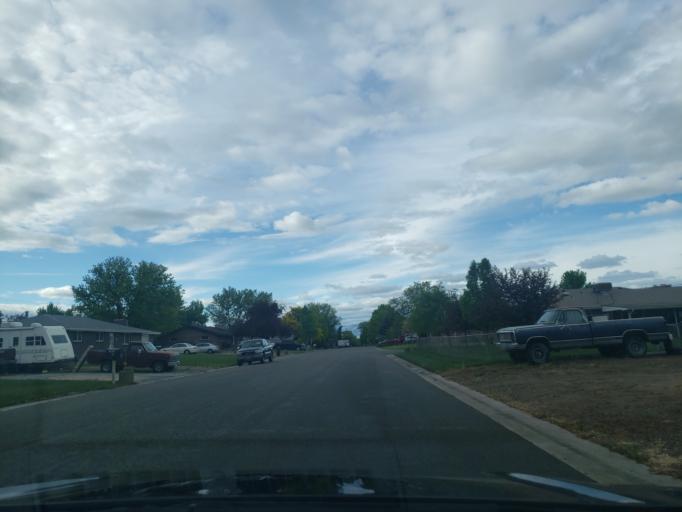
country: US
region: Colorado
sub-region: Mesa County
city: Redlands
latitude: 39.0938
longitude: -108.6588
